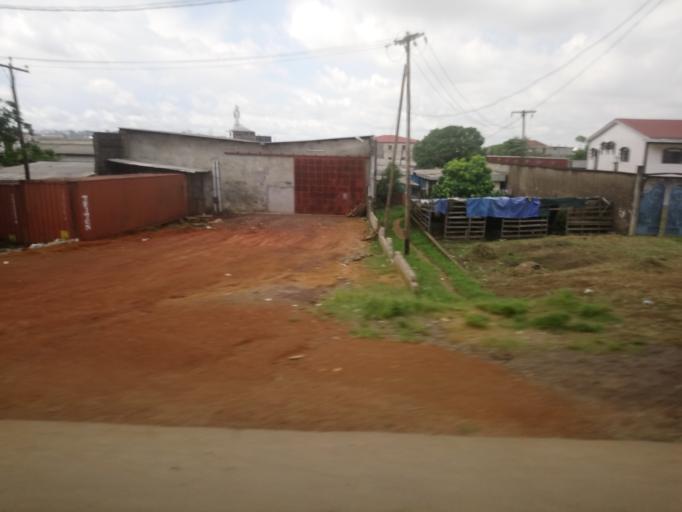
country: CM
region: Littoral
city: Douala
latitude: 4.0217
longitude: 9.7210
